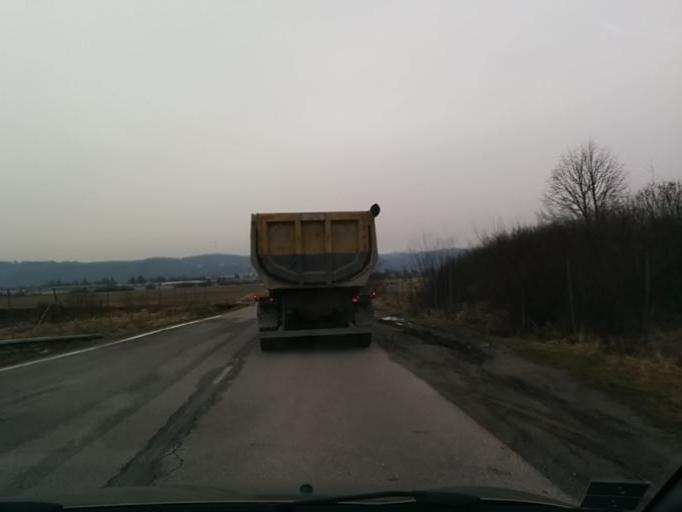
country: SK
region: Banskobystricky
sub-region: Okres Banska Bystrica
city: Zvolen
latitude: 48.6281
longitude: 19.1209
